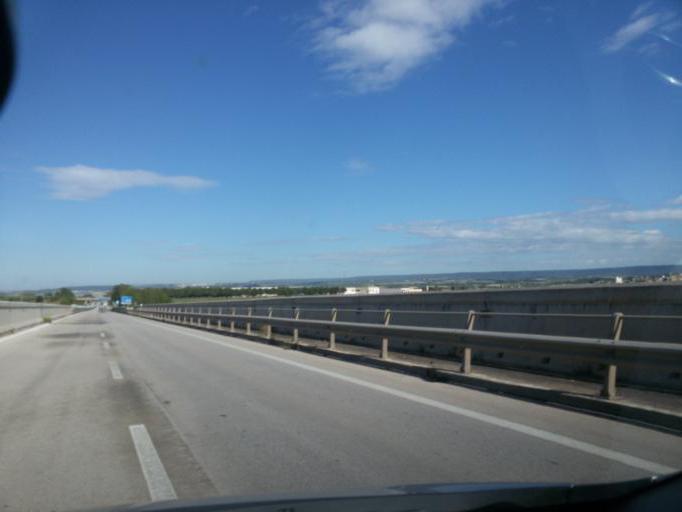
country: IT
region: Apulia
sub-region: Provincia di Taranto
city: Grottaglie
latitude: 40.5232
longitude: 17.4312
